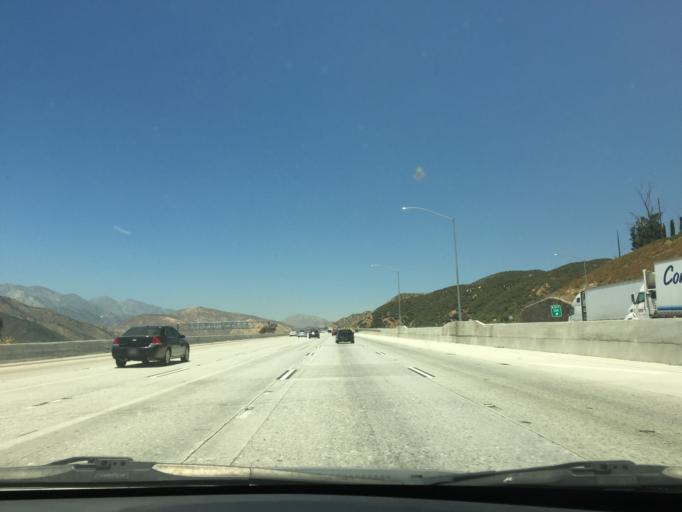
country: US
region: California
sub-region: San Bernardino County
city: Muscoy
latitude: 34.2346
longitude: -117.4220
